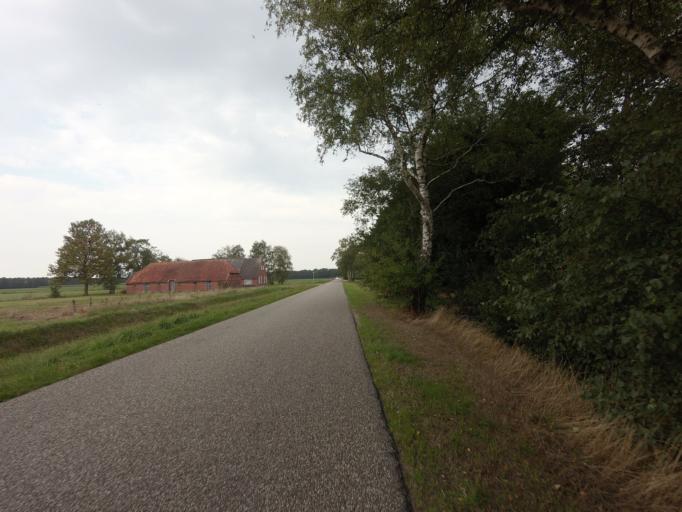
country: NL
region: Drenthe
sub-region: Gemeente Tynaarlo
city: Vries
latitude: 53.0543
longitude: 6.5892
